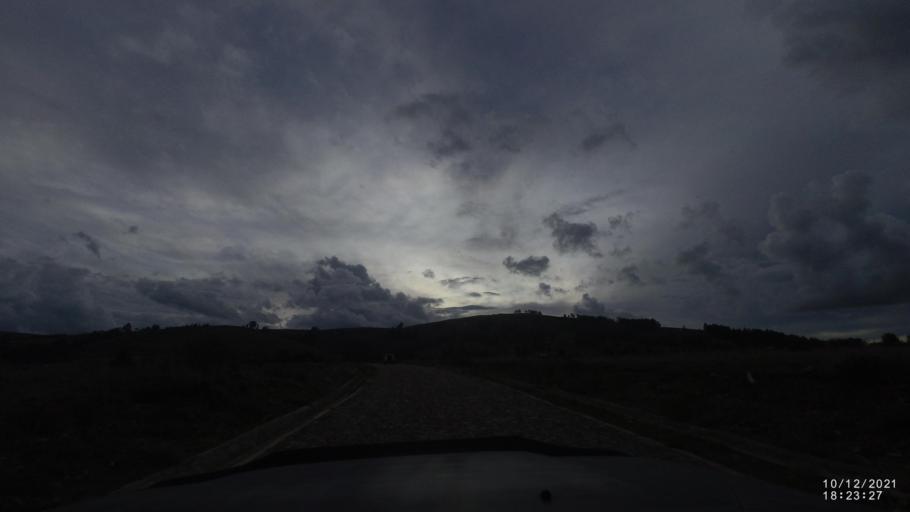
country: BO
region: Cochabamba
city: Tarata
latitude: -17.7861
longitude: -65.9680
